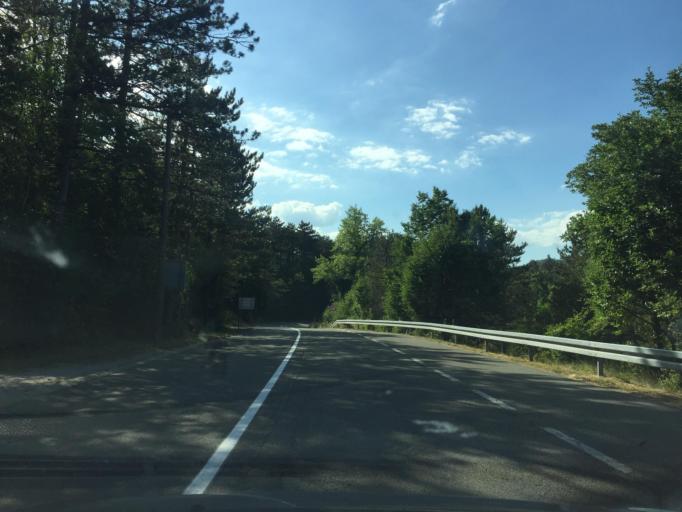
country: HR
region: Primorsko-Goranska
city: Klana
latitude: 45.4357
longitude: 14.3649
